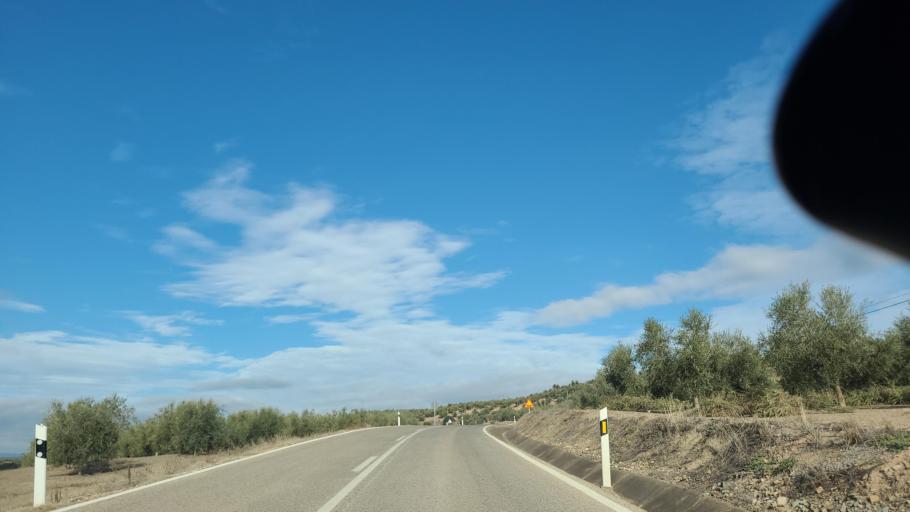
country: ES
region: Andalusia
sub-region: Provincia de Jaen
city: Espeluy
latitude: 38.0177
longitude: -3.8827
